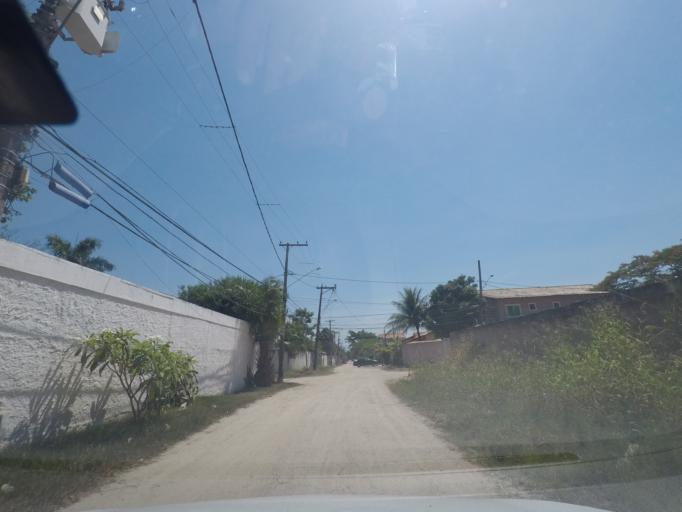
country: BR
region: Rio de Janeiro
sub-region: Niteroi
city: Niteroi
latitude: -22.9346
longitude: -43.0154
